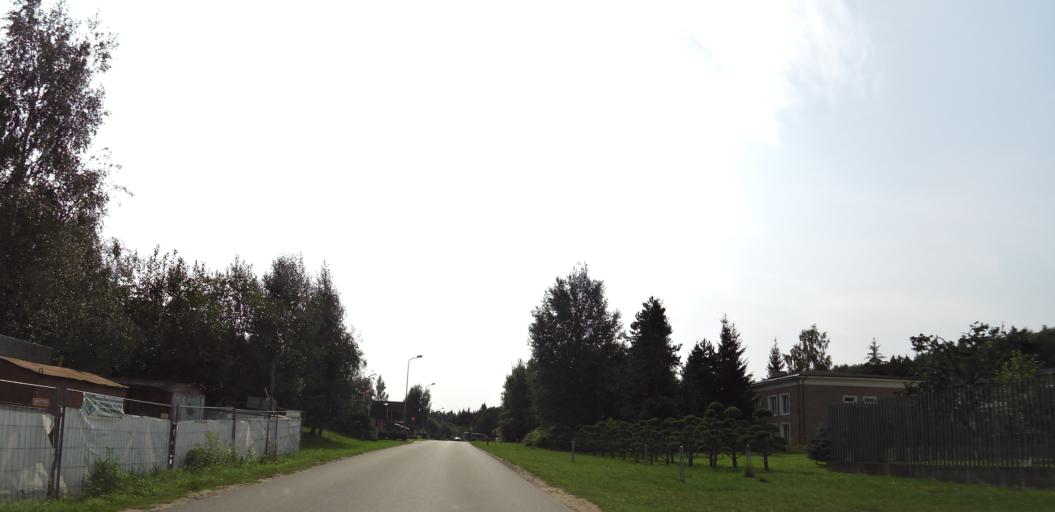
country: LT
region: Vilnius County
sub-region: Vilnius
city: Fabijoniskes
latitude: 54.7472
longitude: 25.2445
